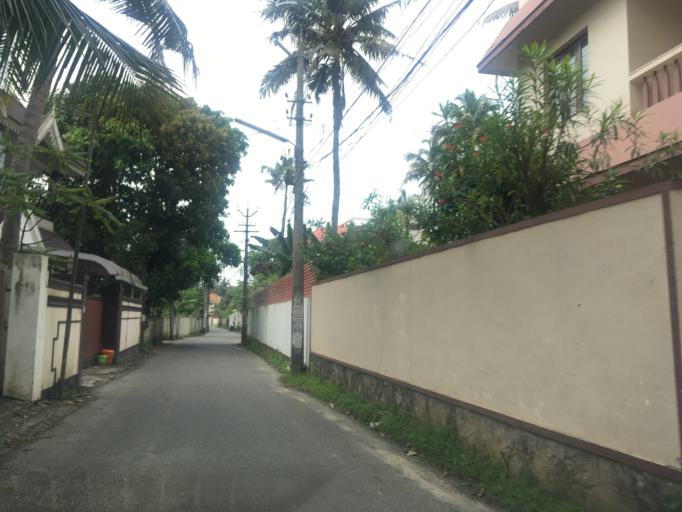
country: IN
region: Kerala
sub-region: Ernakulam
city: Elur
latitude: 10.0338
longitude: 76.3069
